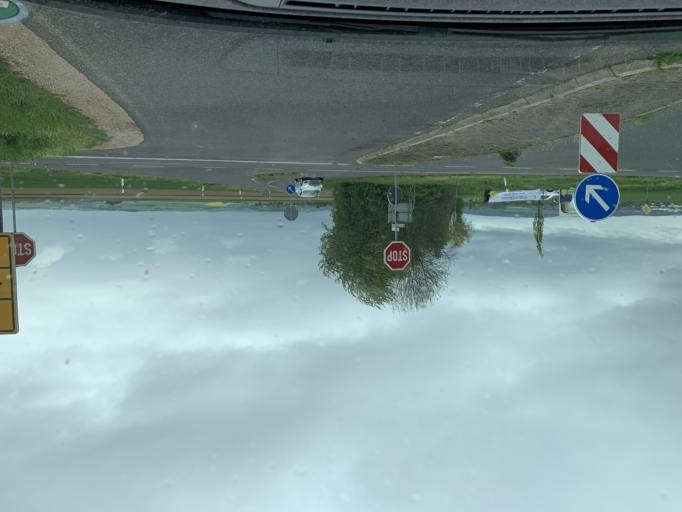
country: DE
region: North Rhine-Westphalia
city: Zulpich
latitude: 50.6779
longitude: 6.6421
